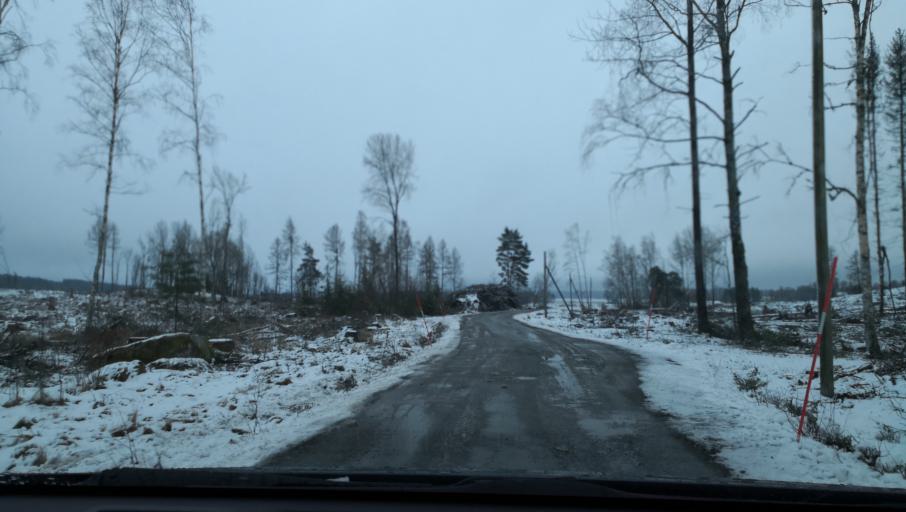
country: SE
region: Vaestmanland
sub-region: Kopings Kommun
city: Kolsva
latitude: 59.5443
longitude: 15.8812
